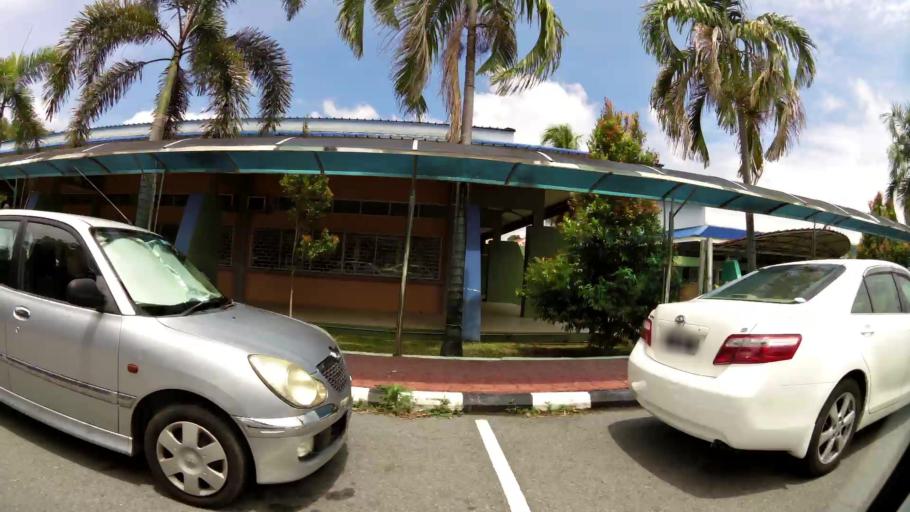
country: BN
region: Brunei and Muara
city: Bandar Seri Begawan
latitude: 4.9022
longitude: 114.9137
